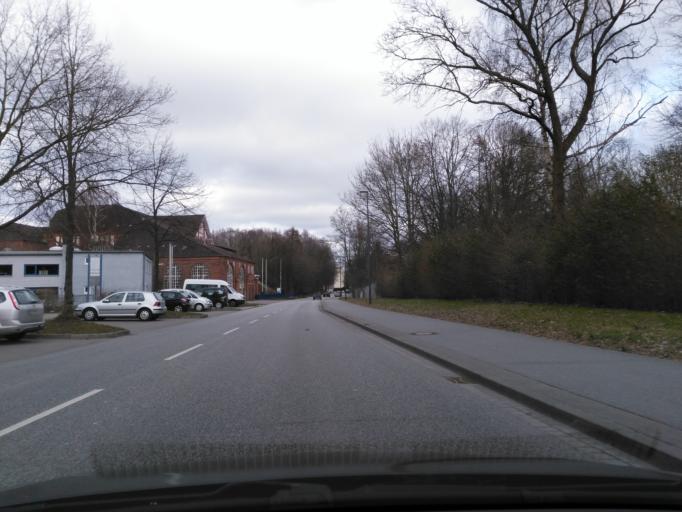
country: DE
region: Schleswig-Holstein
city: Molfsee
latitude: 54.2902
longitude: 10.0926
